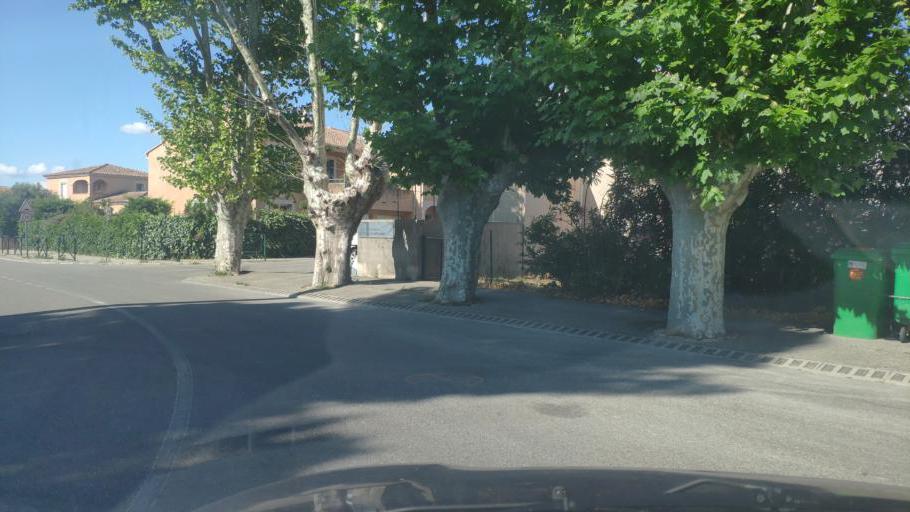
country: FR
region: Provence-Alpes-Cote d'Azur
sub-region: Departement du Vaucluse
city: Entraigues-sur-la-Sorgue
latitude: 43.9979
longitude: 4.9280
